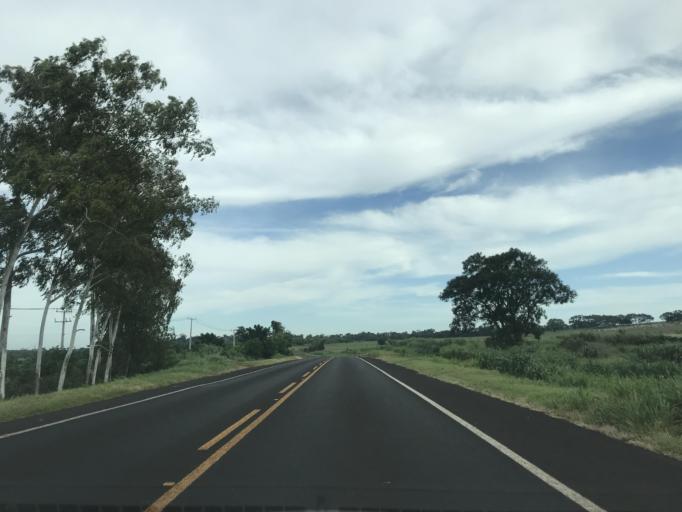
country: BR
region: Parana
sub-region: Paranavai
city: Paranavai
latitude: -23.0296
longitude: -52.4831
